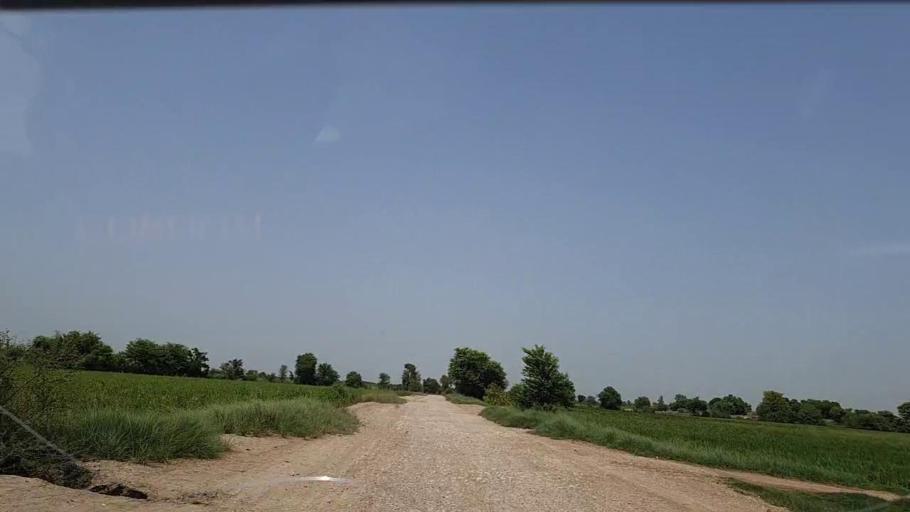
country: PK
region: Sindh
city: Tharu Shah
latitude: 26.9529
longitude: 68.0434
